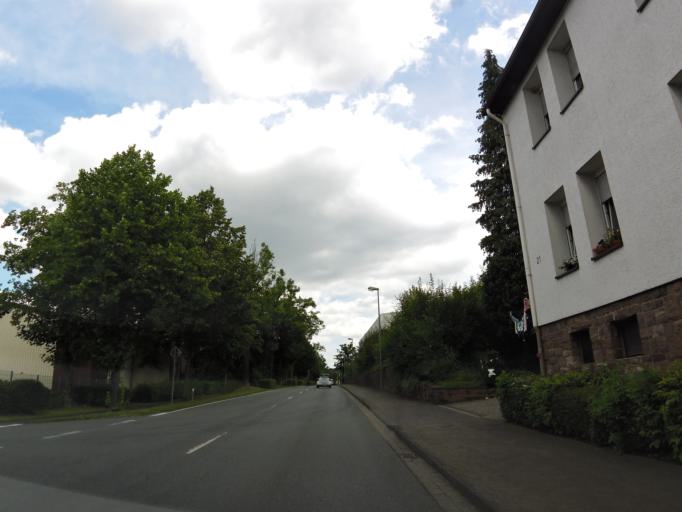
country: DE
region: Lower Saxony
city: Boffzen
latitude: 51.7566
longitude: 9.4024
